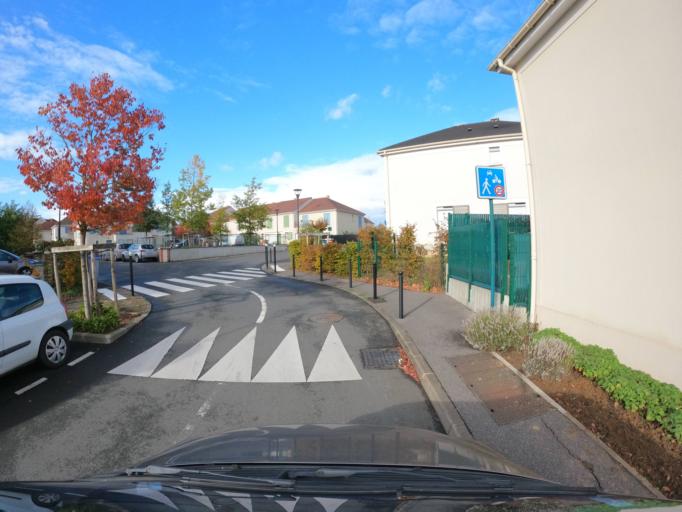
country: FR
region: Ile-de-France
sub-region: Departement de Seine-et-Marne
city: Magny-le-Hongre
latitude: 48.8717
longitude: 2.8179
